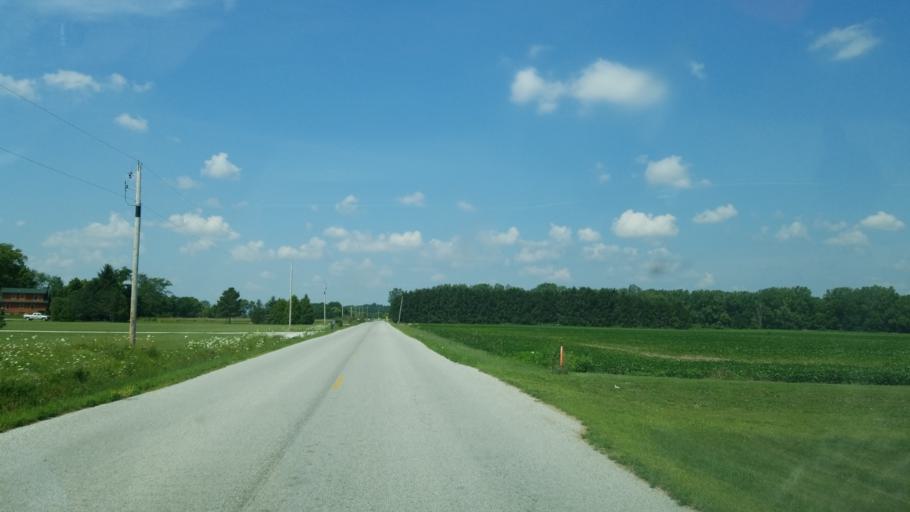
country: US
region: Ohio
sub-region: Seneca County
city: Fostoria
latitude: 41.2385
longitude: -83.5277
